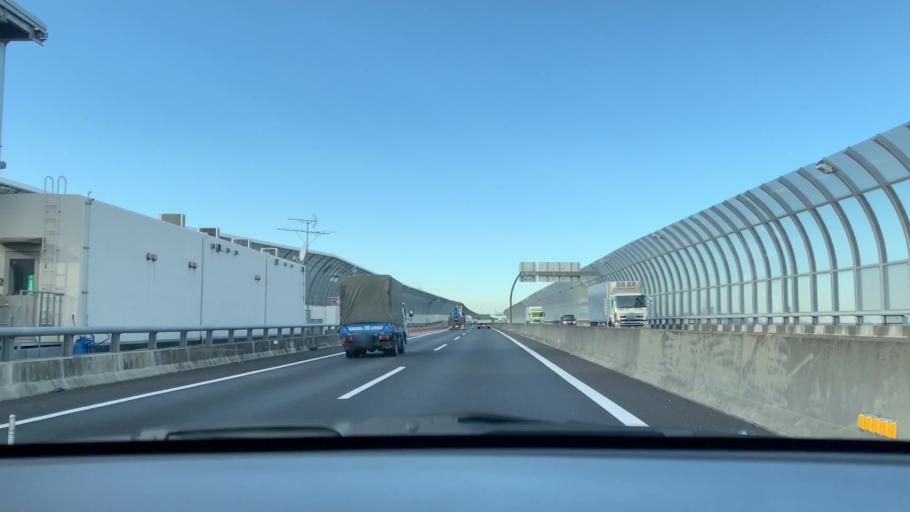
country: JP
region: Chiba
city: Matsudo
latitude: 35.8038
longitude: 139.8773
